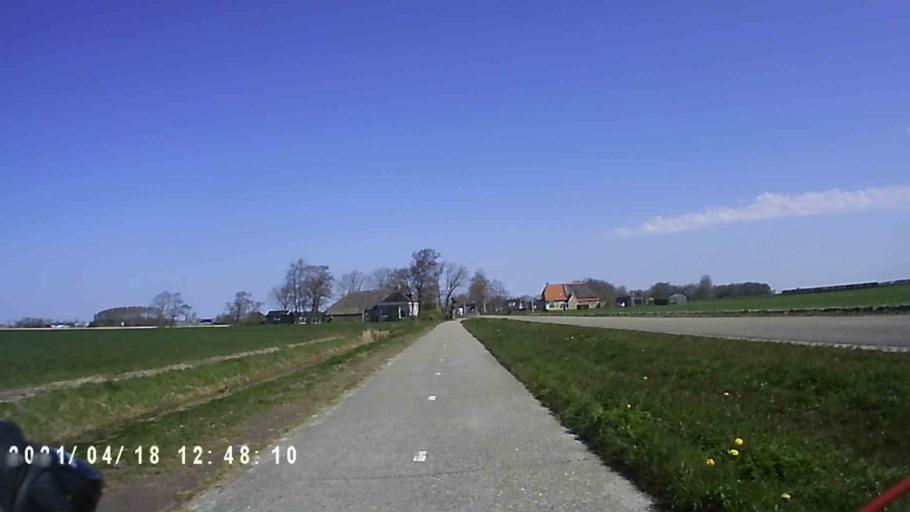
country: NL
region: Friesland
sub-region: Gemeente Dongeradeel
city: Dokkum
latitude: 53.3724
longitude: 6.0508
